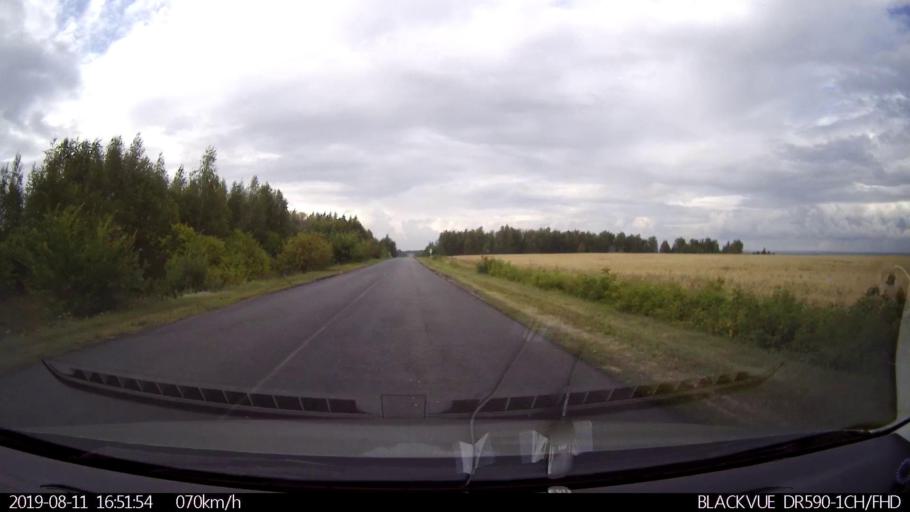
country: RU
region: Ulyanovsk
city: Mayna
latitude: 54.2420
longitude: 47.6757
